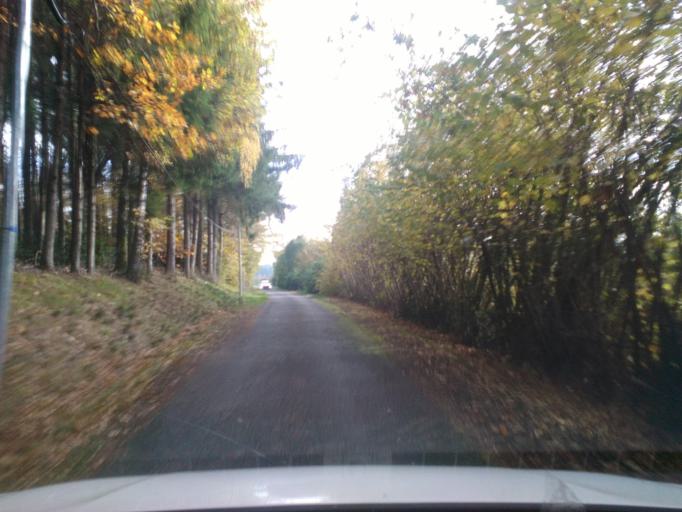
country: FR
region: Lorraine
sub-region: Departement des Vosges
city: Moyenmoutier
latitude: 48.3616
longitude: 6.8942
